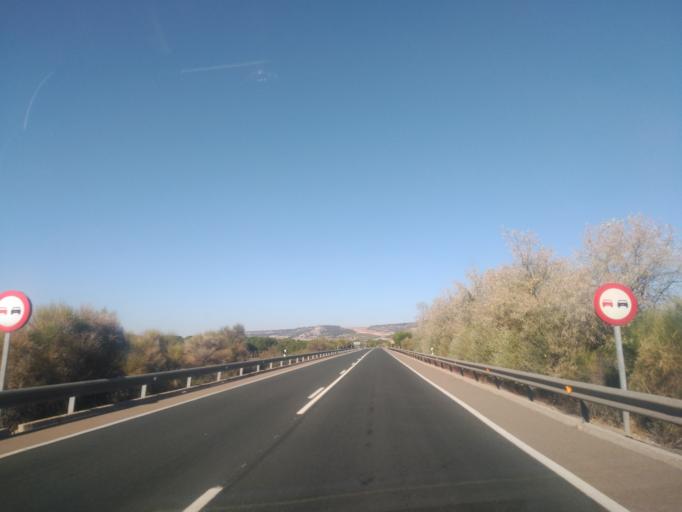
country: ES
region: Castille and Leon
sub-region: Provincia de Valladolid
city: Quintanilla de Onesimo
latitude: 41.6206
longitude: -4.3738
